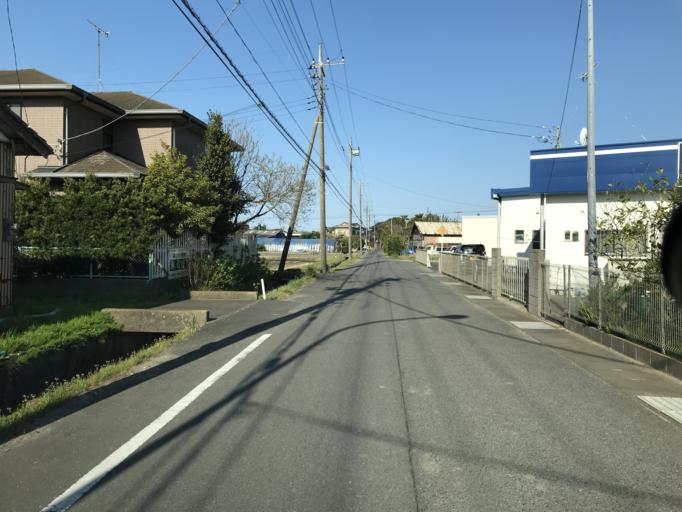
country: JP
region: Chiba
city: Omigawa
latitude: 35.8399
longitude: 140.5993
